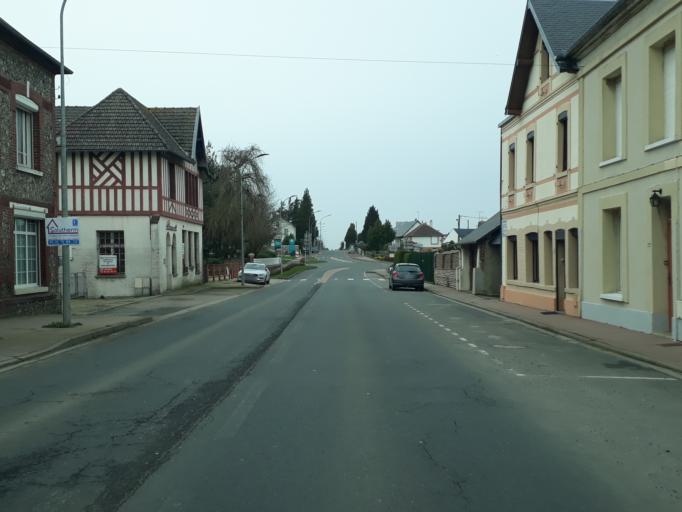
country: FR
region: Haute-Normandie
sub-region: Departement de la Seine-Maritime
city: Breaute
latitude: 49.6268
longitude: 0.3988
